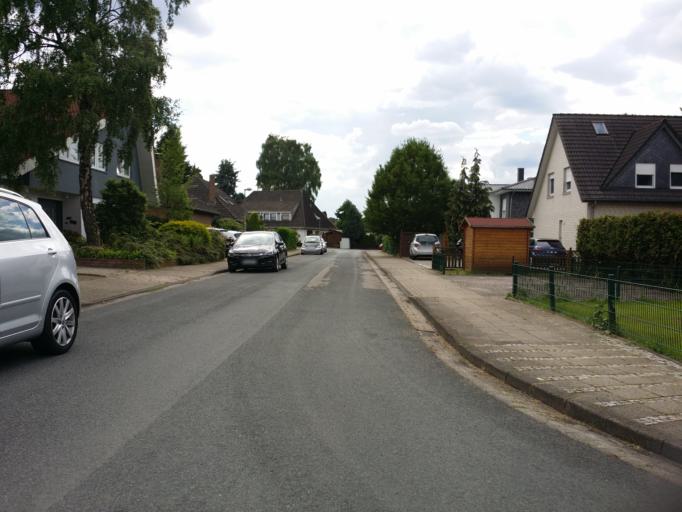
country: DE
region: Lower Saxony
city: Stuhr
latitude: 53.0365
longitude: 8.6932
